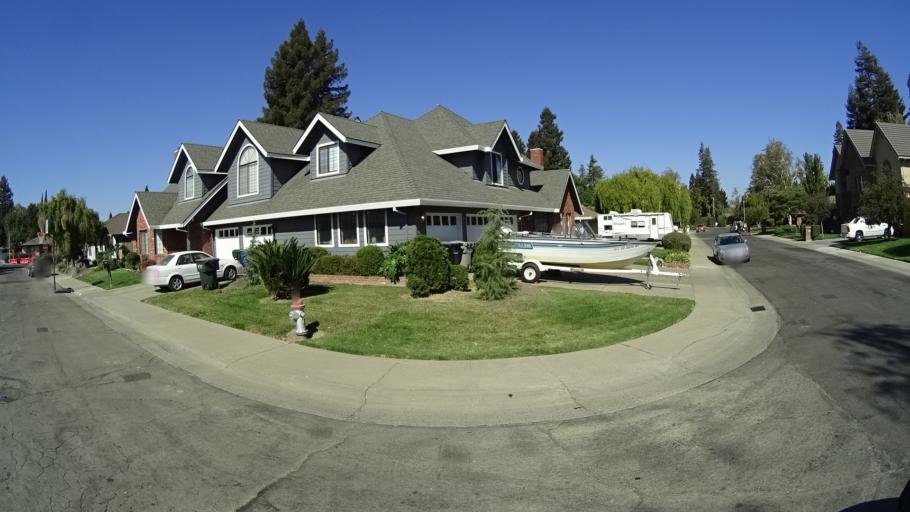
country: US
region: California
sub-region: Sacramento County
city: Parkway
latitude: 38.4957
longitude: -121.5305
